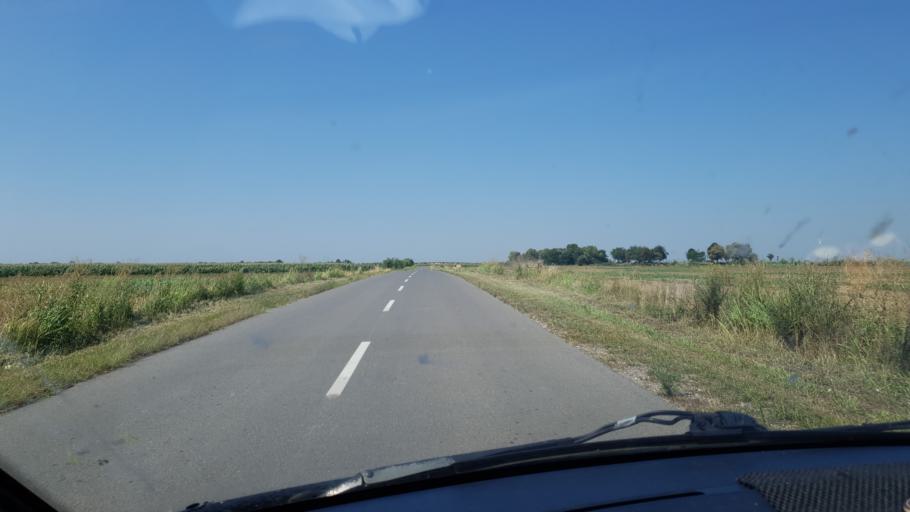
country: RS
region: Autonomna Pokrajina Vojvodina
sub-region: Juznobacki Okrug
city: Kovilj
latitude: 45.2124
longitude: 20.0641
